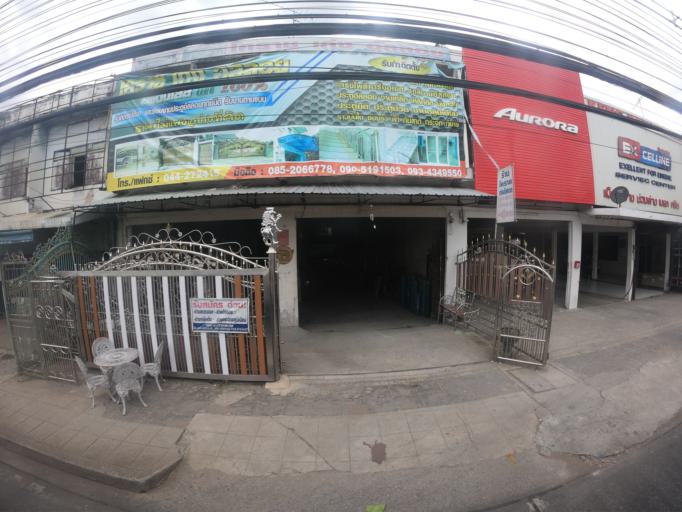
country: TH
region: Nakhon Ratchasima
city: Nakhon Ratchasima
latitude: 14.9801
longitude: 102.1065
